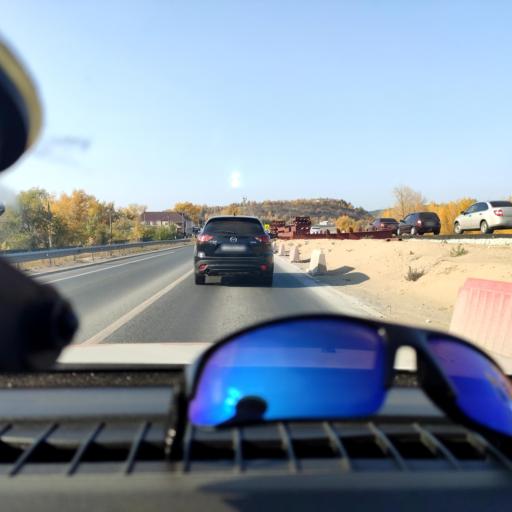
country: RU
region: Samara
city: Volzhskiy
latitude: 53.4141
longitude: 50.1337
